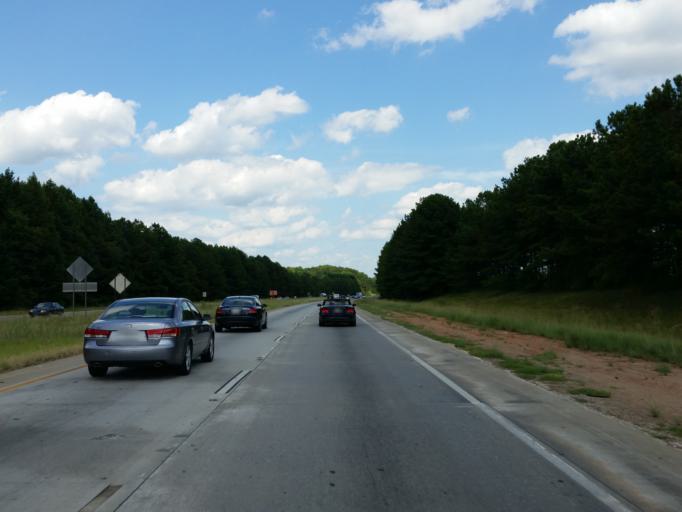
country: US
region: Georgia
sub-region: Gwinnett County
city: Lawrenceville
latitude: 33.9834
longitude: -83.9636
